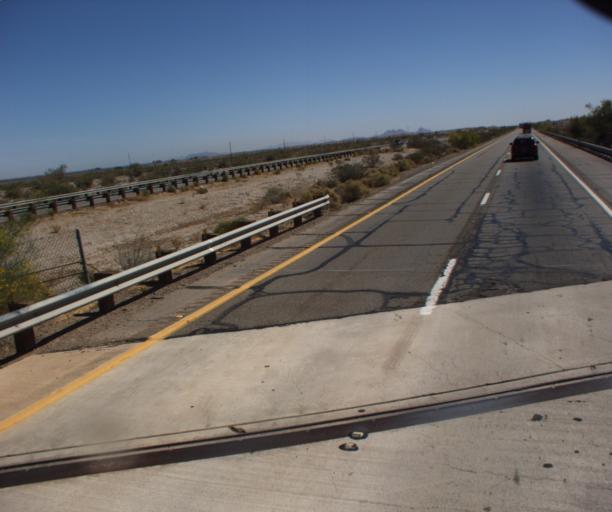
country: US
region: Arizona
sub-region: Yuma County
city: Wellton
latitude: 32.6591
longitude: -114.2521
